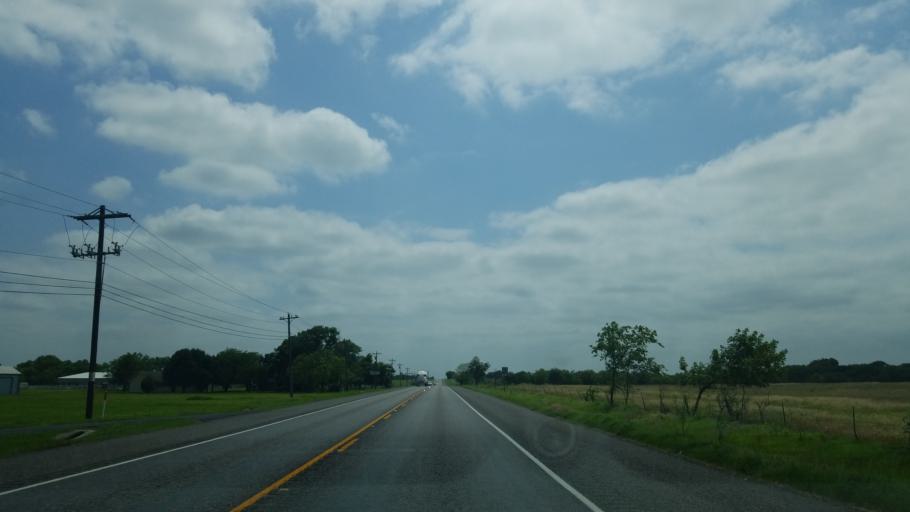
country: US
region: Texas
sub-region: Denton County
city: Krugerville
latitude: 33.3061
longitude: -97.0629
